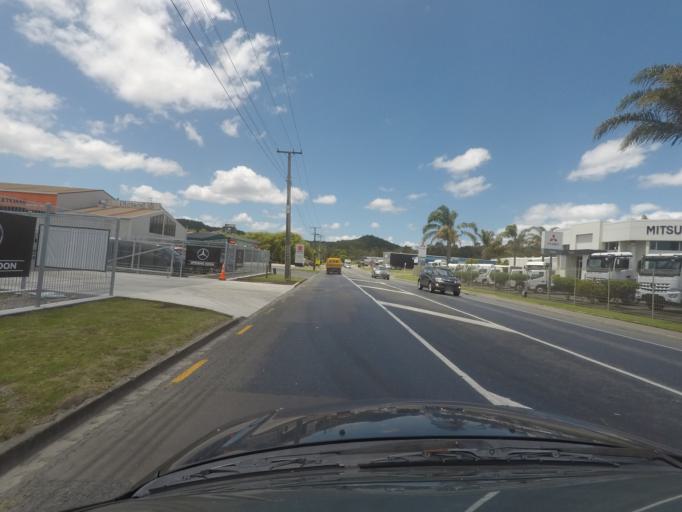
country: NZ
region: Northland
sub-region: Whangarei
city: Whangarei
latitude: -35.7521
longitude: 174.3153
